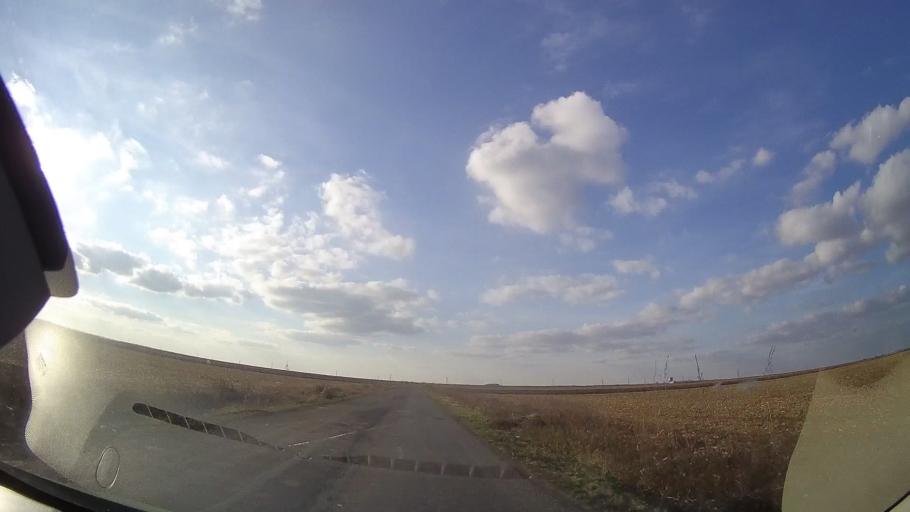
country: RO
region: Constanta
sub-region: Comuna Cerchezu
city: Cerchezu
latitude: 43.8255
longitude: 28.1311
